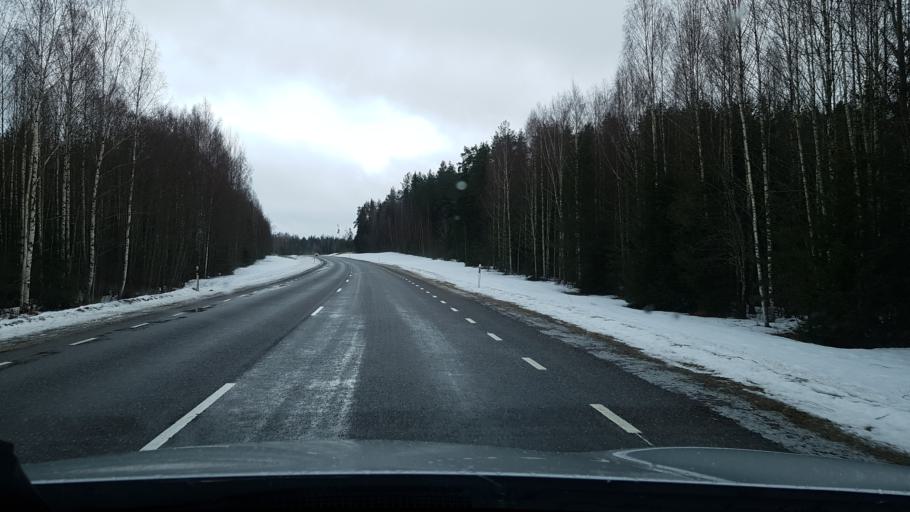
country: LV
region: Apes Novads
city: Ape
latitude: 57.6296
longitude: 26.6369
